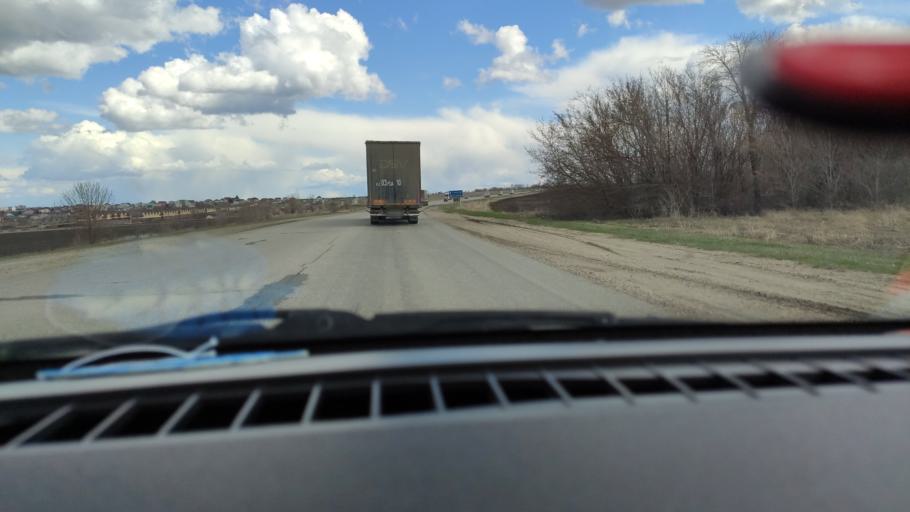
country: RU
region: Samara
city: Varlamovo
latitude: 53.1155
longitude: 48.3465
